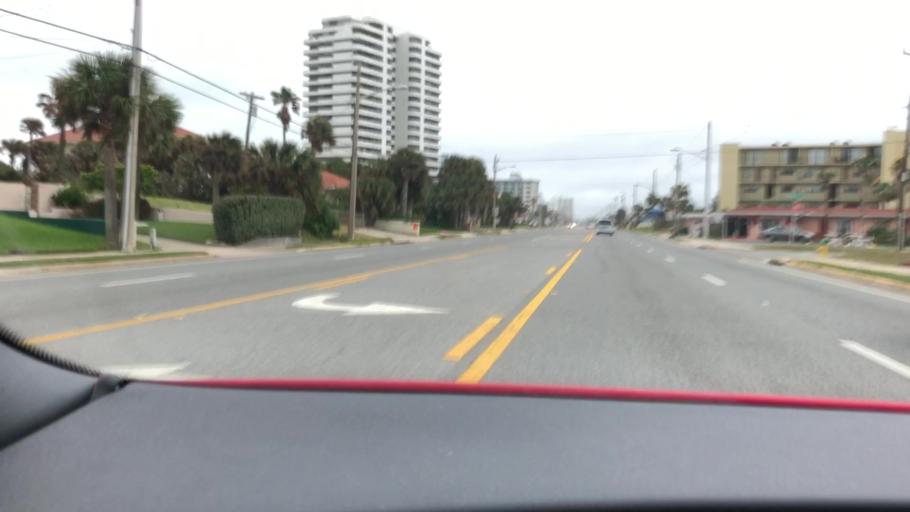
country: US
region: Florida
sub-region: Volusia County
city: Holly Hill
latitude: 29.2519
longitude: -81.0203
